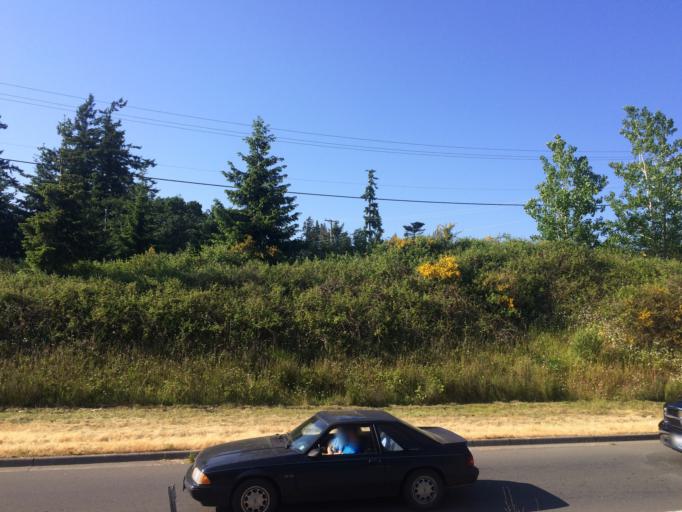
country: CA
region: British Columbia
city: Colwood
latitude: 48.4630
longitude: -123.4502
